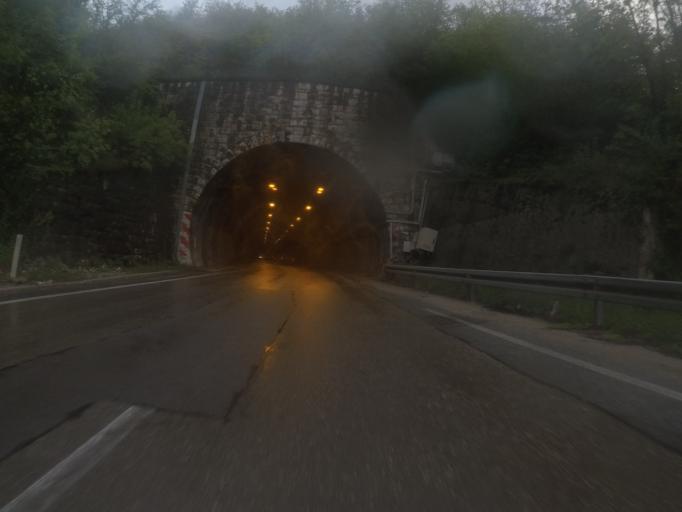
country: BA
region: Federation of Bosnia and Herzegovina
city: Jablanica
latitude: 43.6686
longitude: 17.7778
